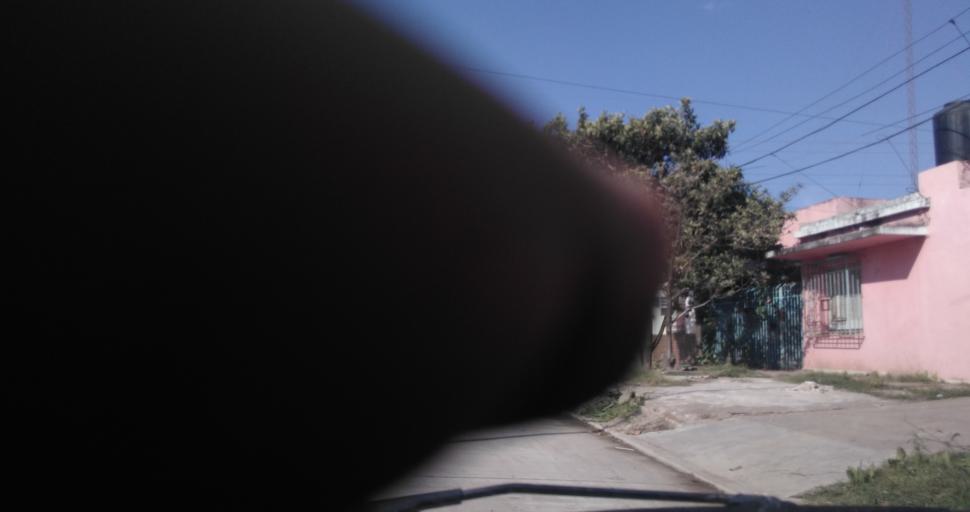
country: AR
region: Chaco
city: Resistencia
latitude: -27.4669
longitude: -58.9664
